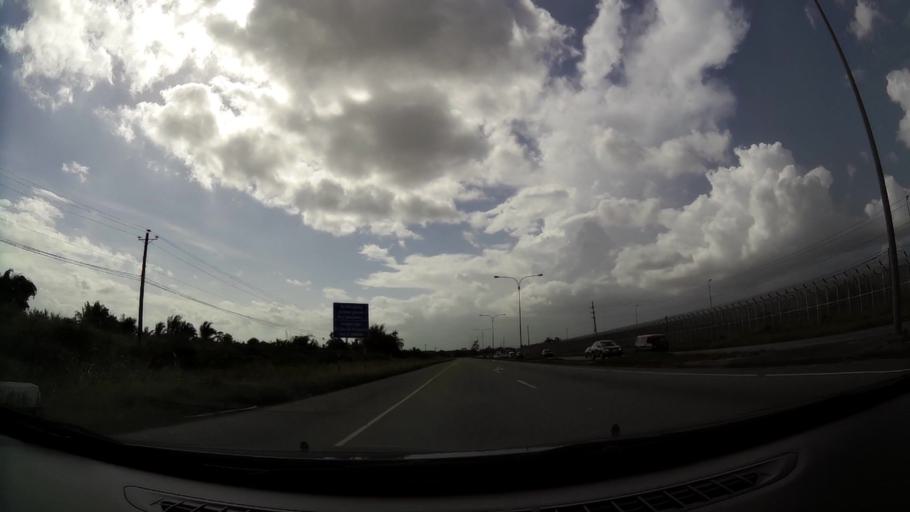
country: TT
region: Tunapuna/Piarco
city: Arouca
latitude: 10.6145
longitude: -61.3324
